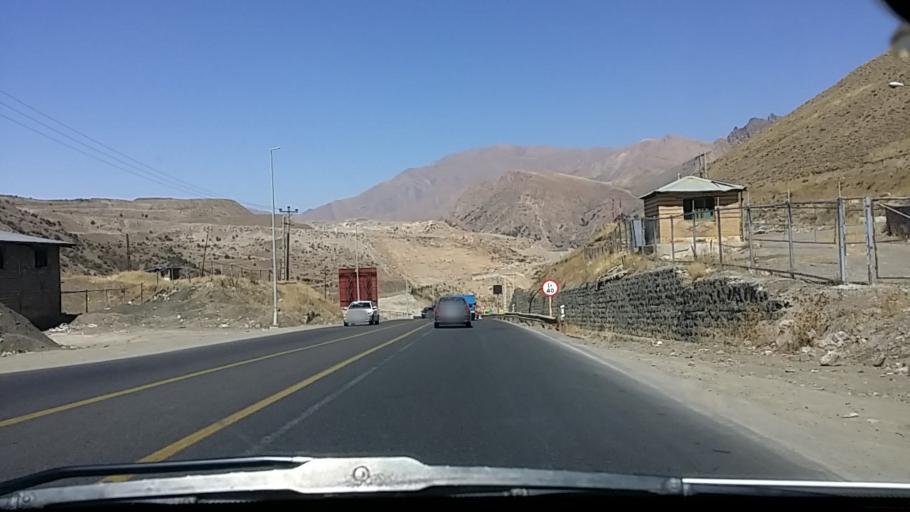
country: IR
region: Tehran
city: Tajrish
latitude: 36.1924
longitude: 51.3199
